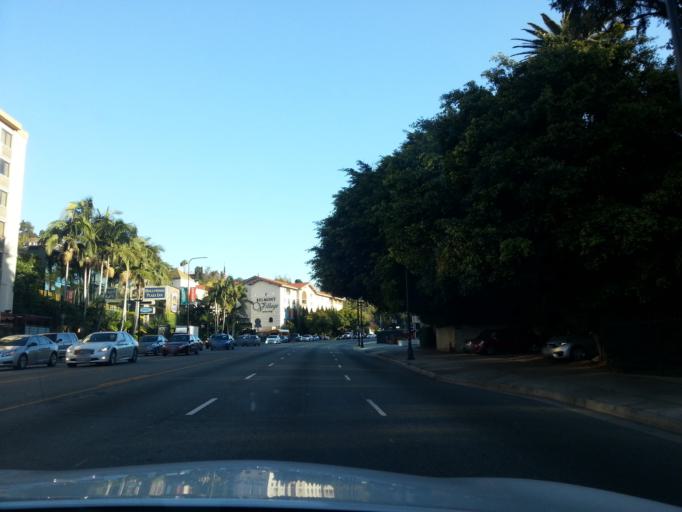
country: US
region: California
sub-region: Los Angeles County
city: Hollywood
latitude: 34.1064
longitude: -118.3374
